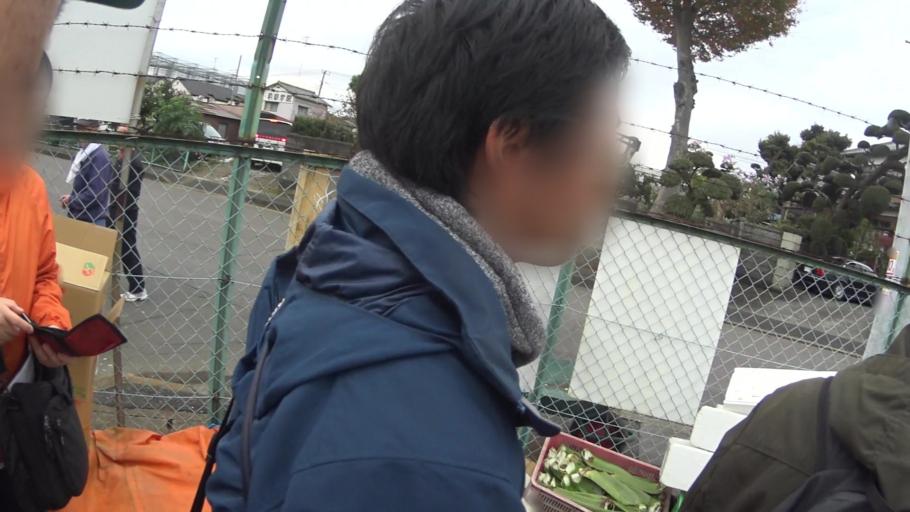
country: JP
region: Chiba
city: Nagareyama
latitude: 35.8404
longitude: 139.8836
